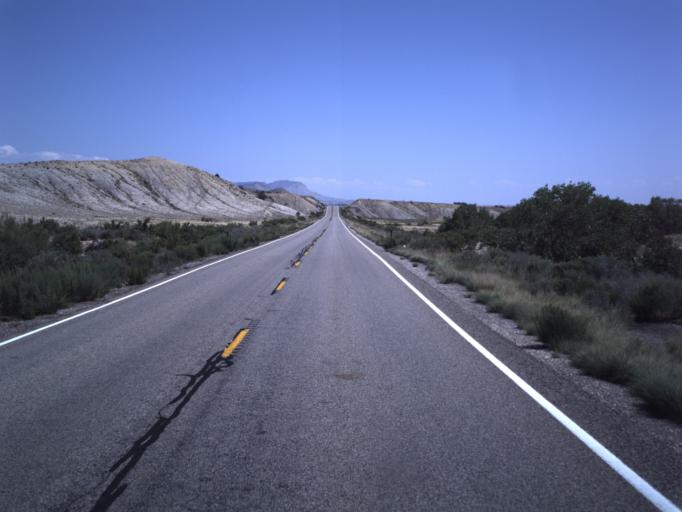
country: US
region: Utah
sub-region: Emery County
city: Ferron
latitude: 38.7903
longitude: -111.3485
